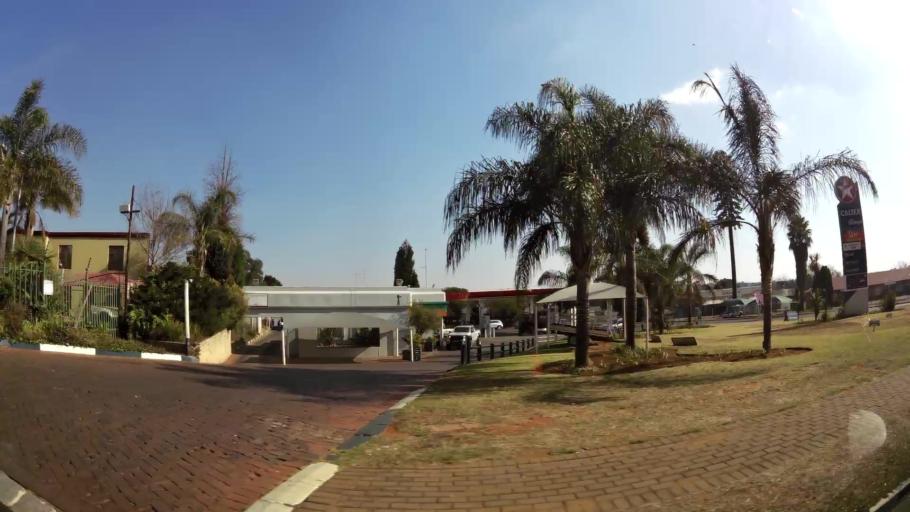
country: ZA
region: Gauteng
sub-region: West Rand District Municipality
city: Randfontein
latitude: -26.1604
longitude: 27.6935
